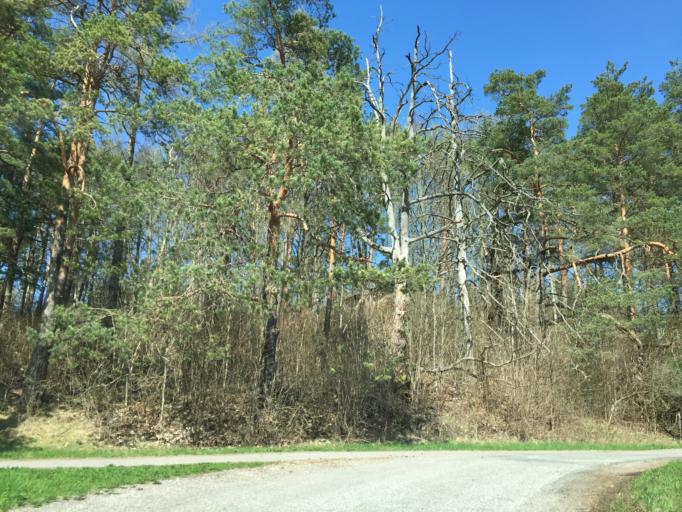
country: EE
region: Tartu
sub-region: Elva linn
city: Elva
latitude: 58.1532
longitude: 26.2266
